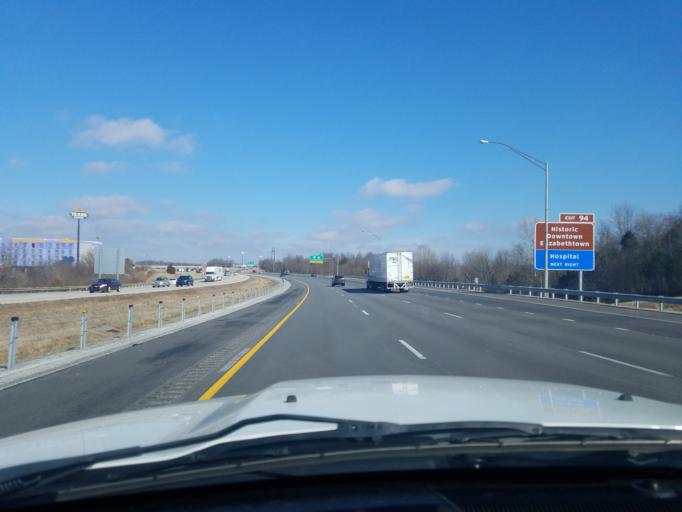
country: US
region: Kentucky
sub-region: Hardin County
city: Elizabethtown
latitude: 37.7065
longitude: -85.8311
